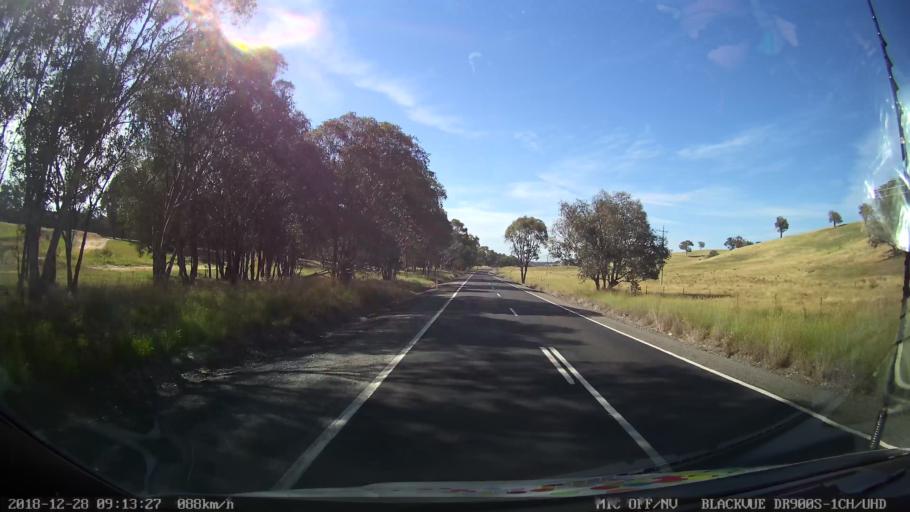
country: AU
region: New South Wales
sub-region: Upper Lachlan Shire
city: Crookwell
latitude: -34.2690
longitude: 149.3435
